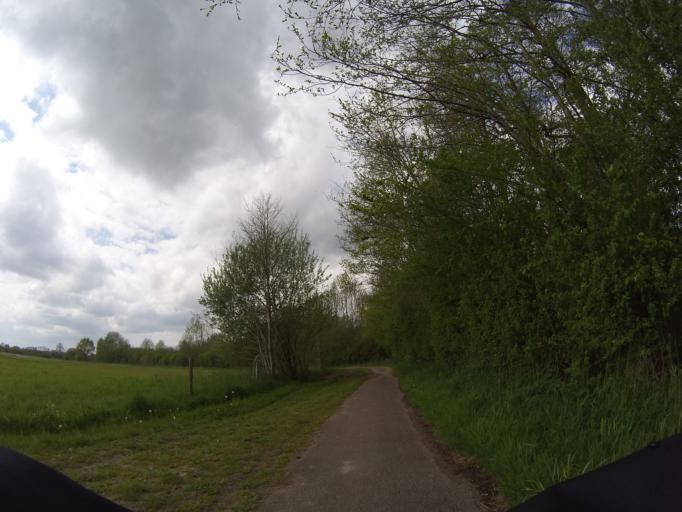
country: NL
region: Overijssel
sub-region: Gemeente Hardenberg
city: Hardenberg
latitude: 52.5329
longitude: 6.5717
